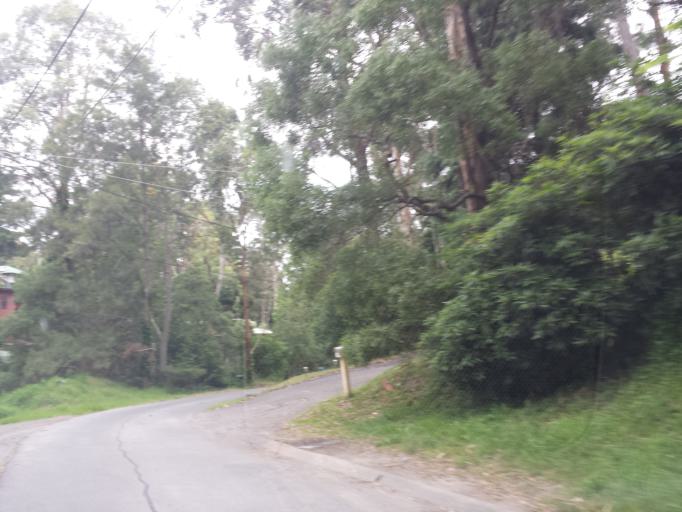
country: AU
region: Victoria
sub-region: Yarra Ranges
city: Belgrave Heights
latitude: -37.9129
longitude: 145.3420
